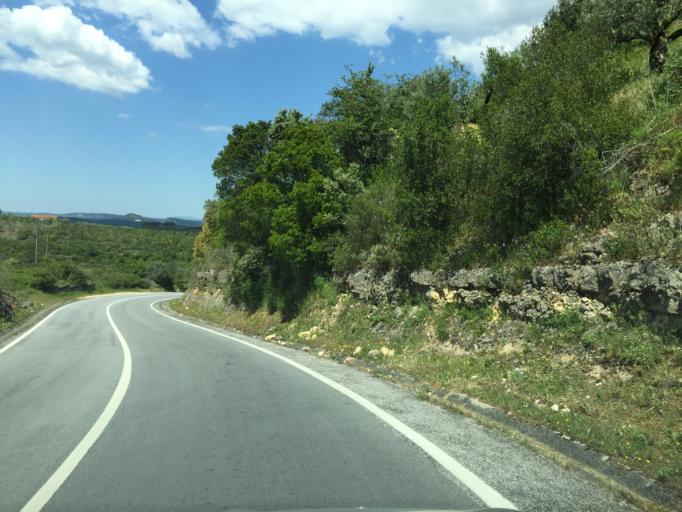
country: PT
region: Santarem
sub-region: Ourem
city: Fatima
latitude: 39.6308
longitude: -8.6582
